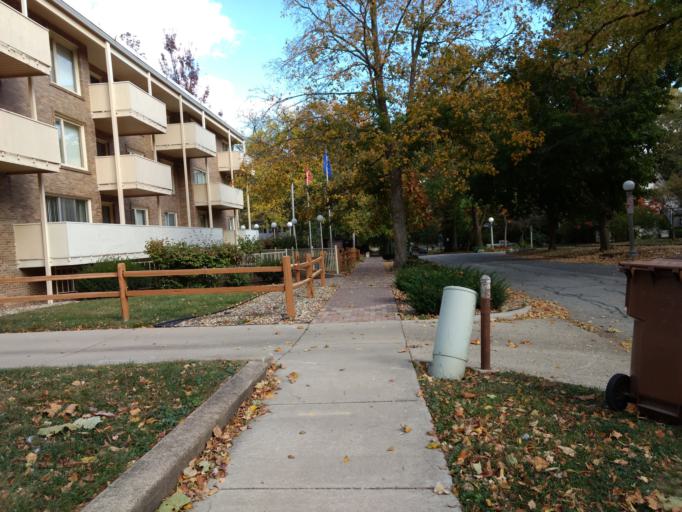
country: US
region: Illinois
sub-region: Champaign County
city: Urbana
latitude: 40.1075
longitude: -88.2183
